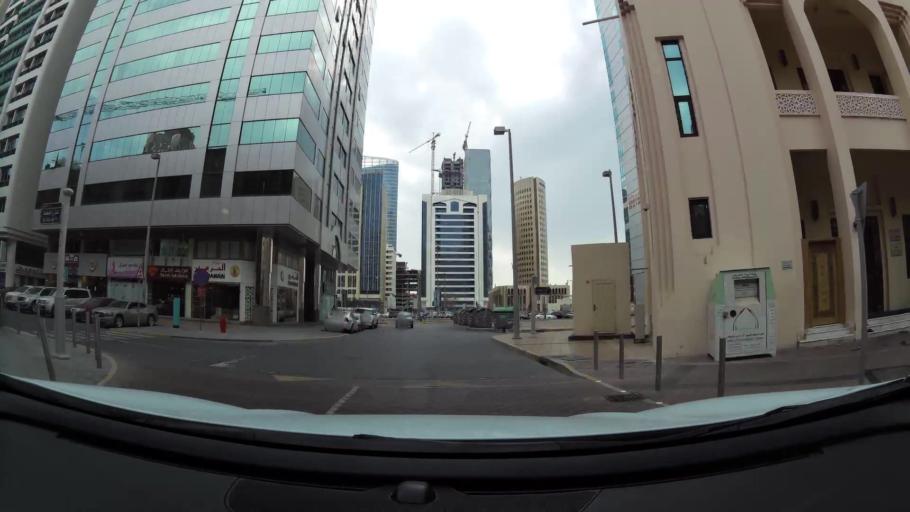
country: AE
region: Abu Dhabi
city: Abu Dhabi
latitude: 24.4896
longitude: 54.3552
